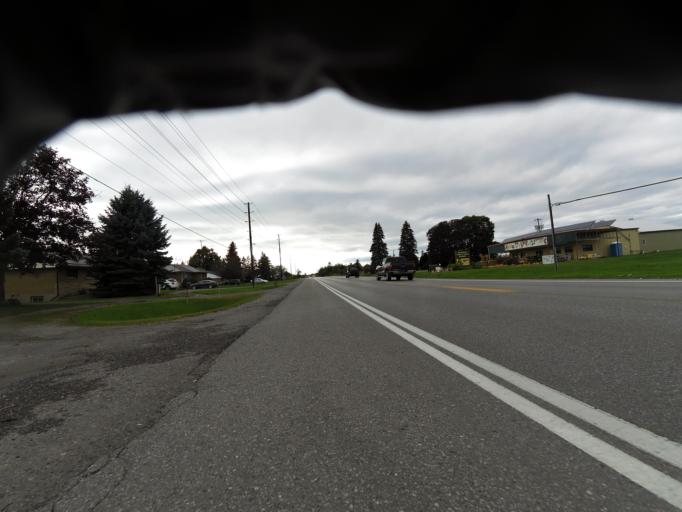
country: CA
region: Ontario
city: Cobourg
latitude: 43.9663
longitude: -78.2209
